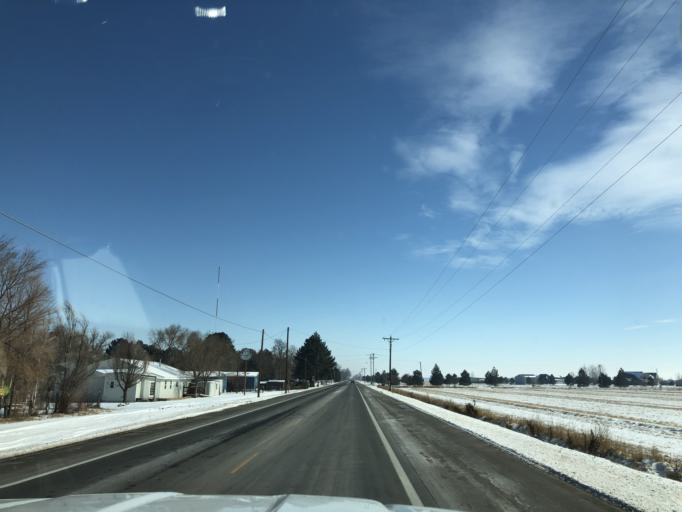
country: US
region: Colorado
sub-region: Morgan County
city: Fort Morgan
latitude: 40.2540
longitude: -103.8515
